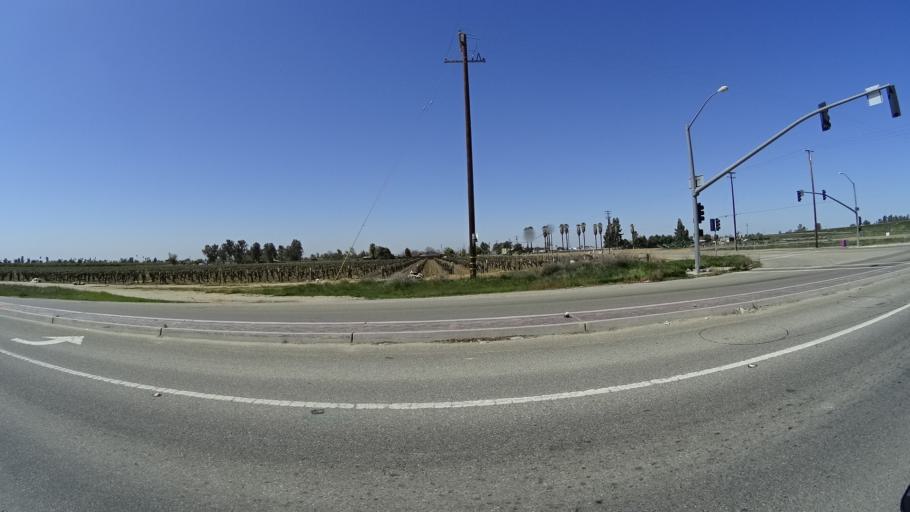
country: US
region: California
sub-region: Fresno County
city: West Park
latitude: 36.7352
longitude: -119.8443
